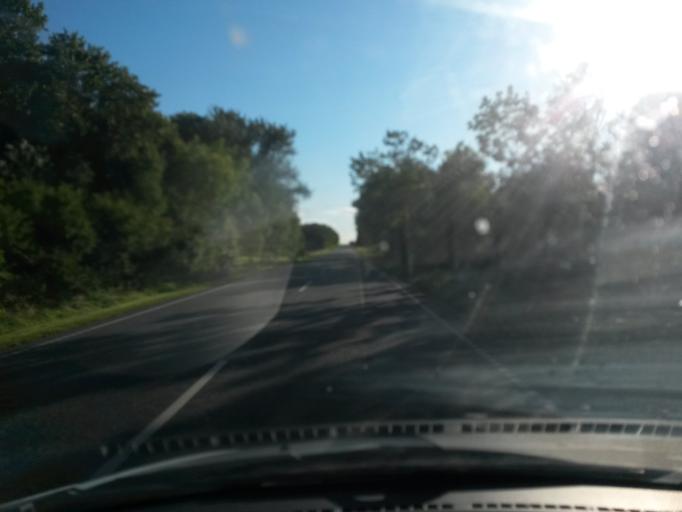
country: DK
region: Central Jutland
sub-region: Silkeborg Kommune
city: Kjellerup
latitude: 56.3083
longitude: 9.5081
